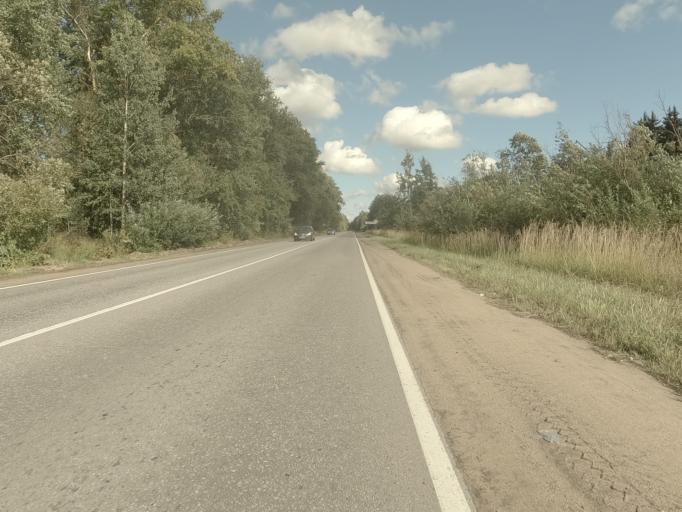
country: RU
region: Leningrad
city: Romanovka
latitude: 60.0243
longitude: 30.7026
